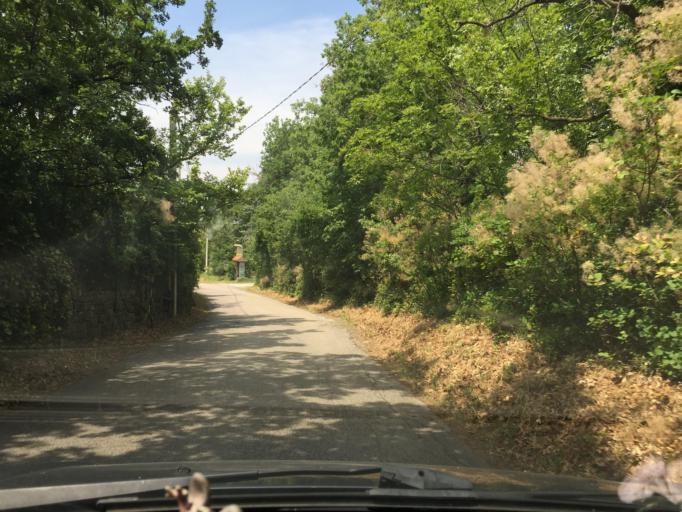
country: IT
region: Friuli Venezia Giulia
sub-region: Provincia di Trieste
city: Domio
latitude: 45.6006
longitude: 13.8173
